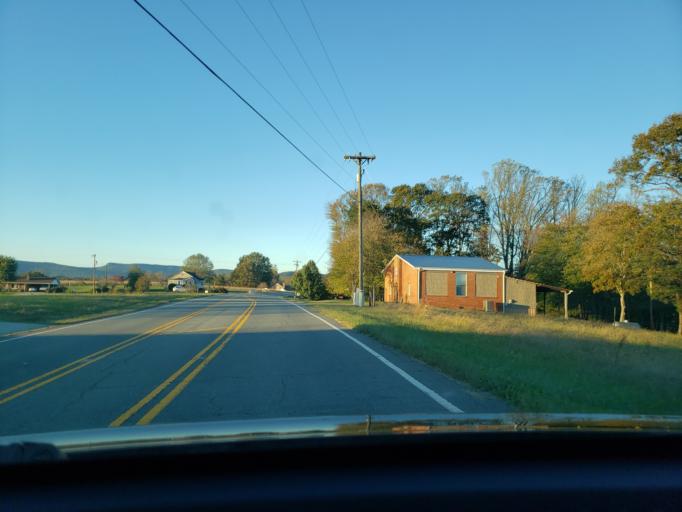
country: US
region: North Carolina
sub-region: Stokes County
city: Danbury
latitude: 36.3294
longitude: -80.2249
